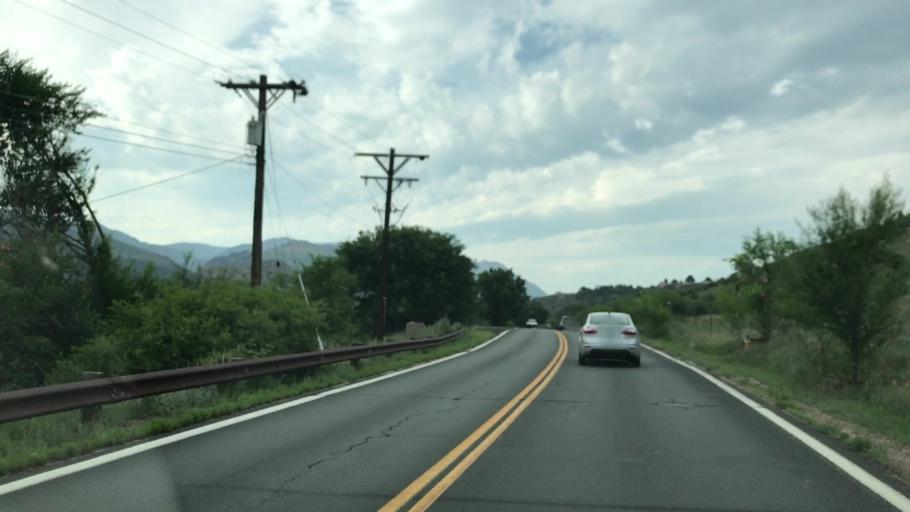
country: US
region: Colorado
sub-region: El Paso County
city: Manitou Springs
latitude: 38.8717
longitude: -104.8682
